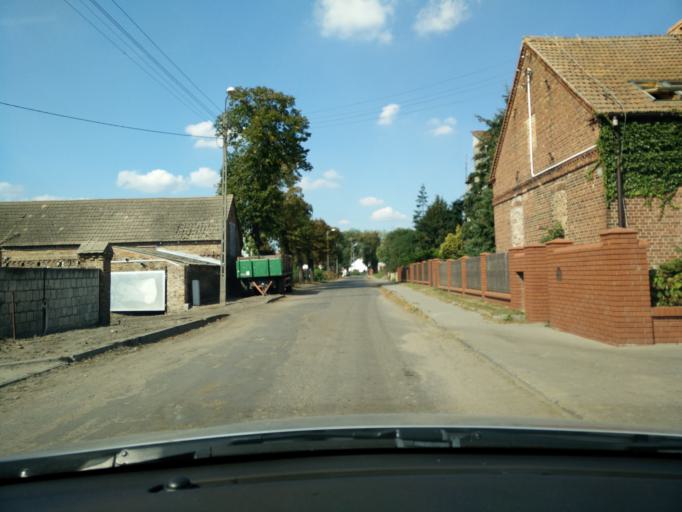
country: PL
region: Greater Poland Voivodeship
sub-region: Powiat poznanski
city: Kleszczewo
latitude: 52.2678
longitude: 17.1714
